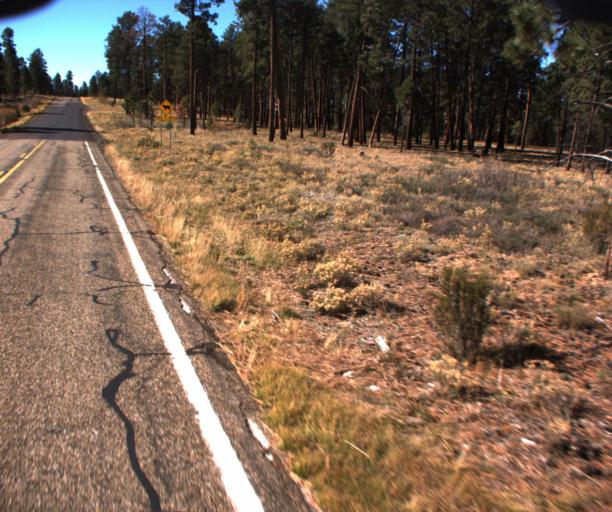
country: US
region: Arizona
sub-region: Coconino County
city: Fredonia
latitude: 36.7687
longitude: -112.2555
